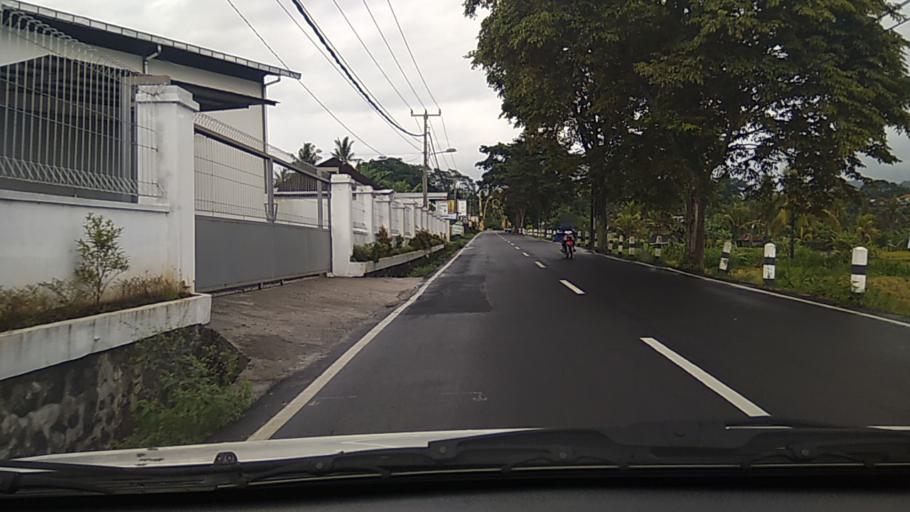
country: ID
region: Bali
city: Banjar Budakeling
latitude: -8.4280
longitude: 115.5924
